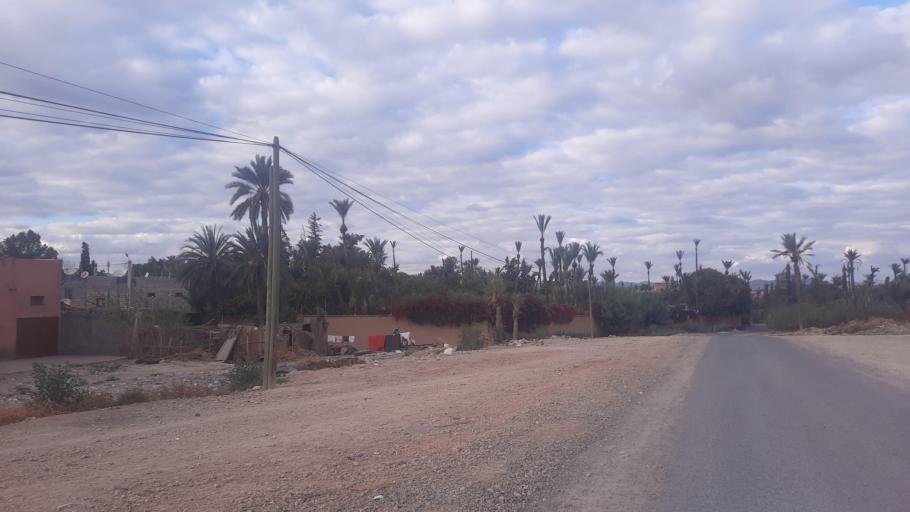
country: MA
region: Marrakech-Tensift-Al Haouz
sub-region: Marrakech
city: Marrakesh
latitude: 31.6726
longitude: -7.9539
